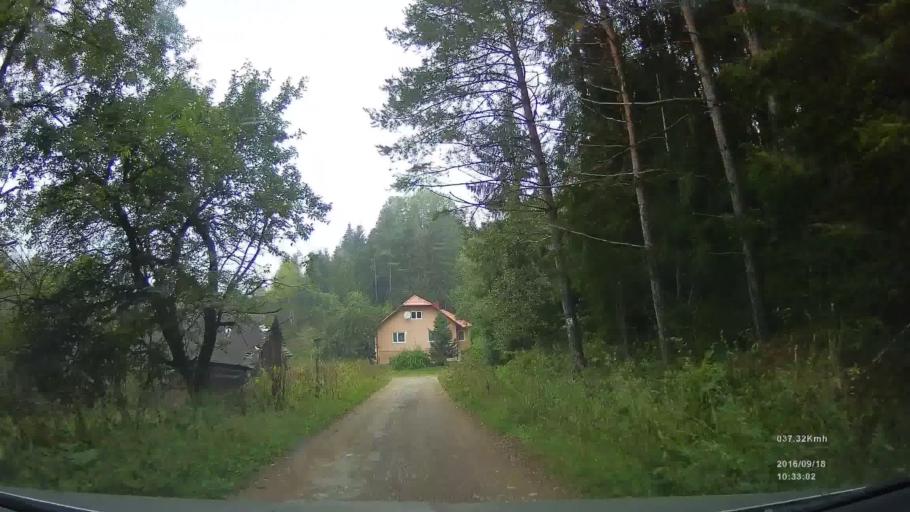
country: SK
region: Presovsky
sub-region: Okres Presov
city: Levoca
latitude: 48.9683
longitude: 20.6206
